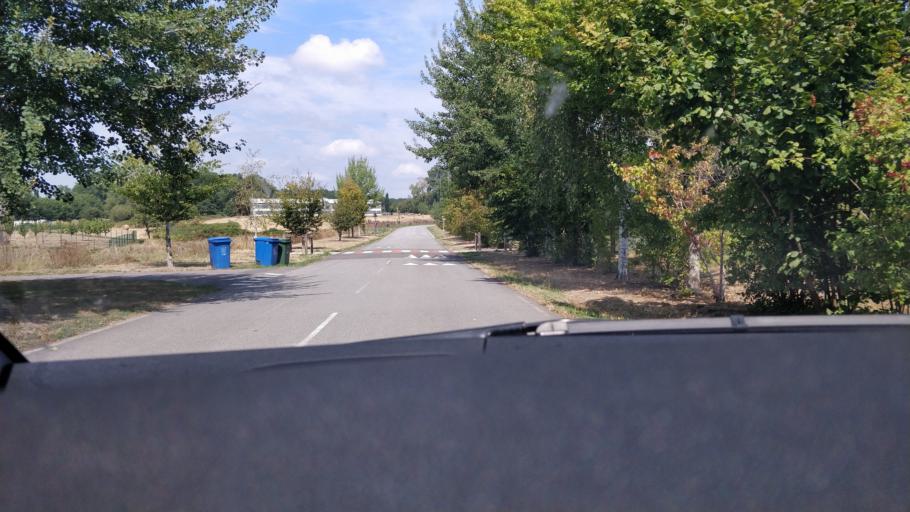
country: FR
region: Limousin
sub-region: Departement de la Haute-Vienne
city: Le Palais-sur-Vienne
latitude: 45.8586
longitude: 1.2990
